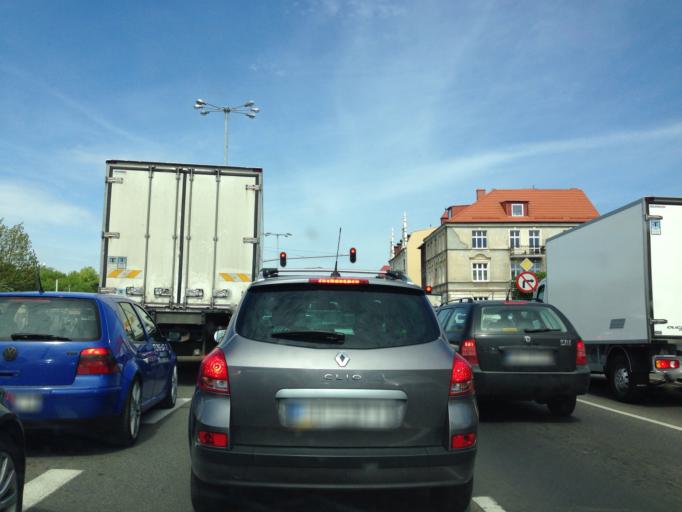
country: PL
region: Pomeranian Voivodeship
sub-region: Sopot
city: Sopot
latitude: 54.4096
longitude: 18.5680
